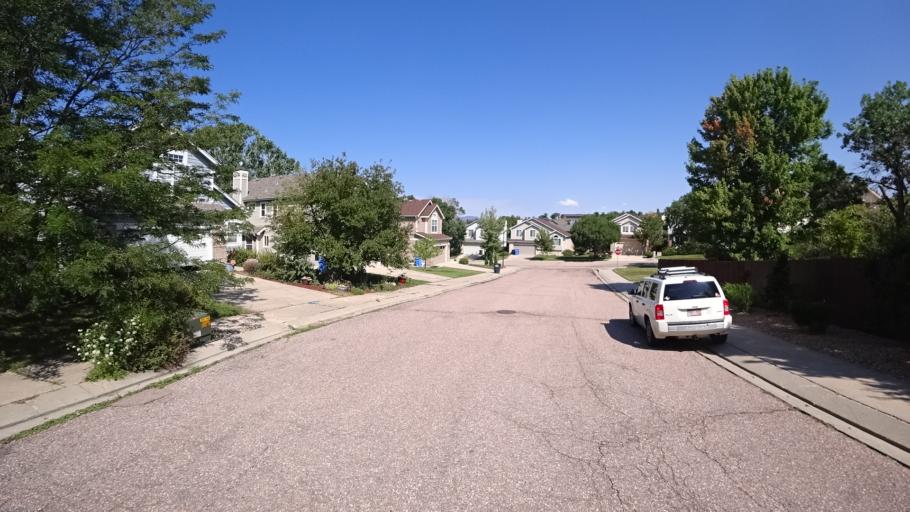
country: US
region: Colorado
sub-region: El Paso County
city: Air Force Academy
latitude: 38.9484
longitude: -104.7872
